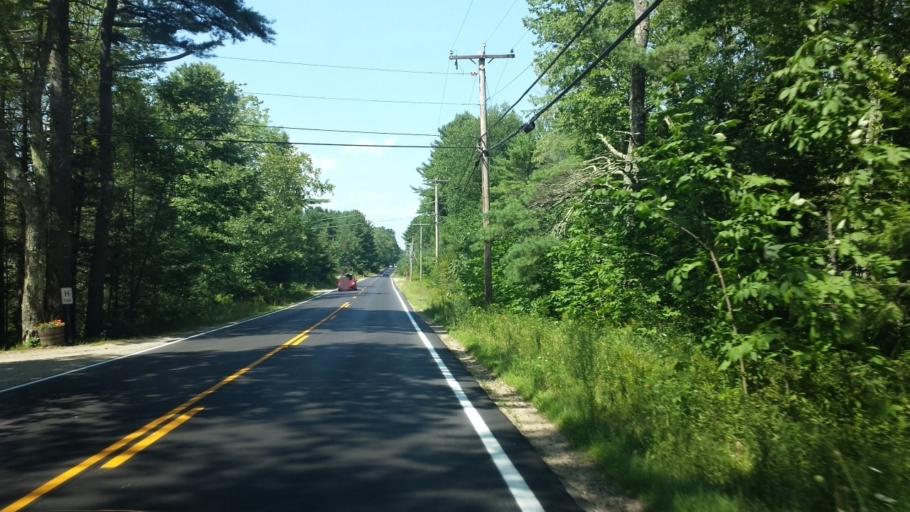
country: US
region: Maine
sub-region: York County
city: Arundel
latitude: 43.3990
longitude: -70.4857
